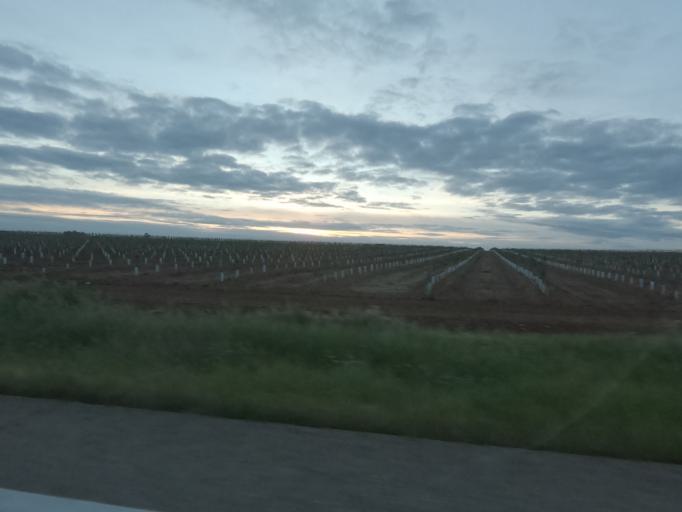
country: ES
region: Extremadura
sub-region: Provincia de Badajoz
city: Badajoz
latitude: 38.9394
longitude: -6.9210
